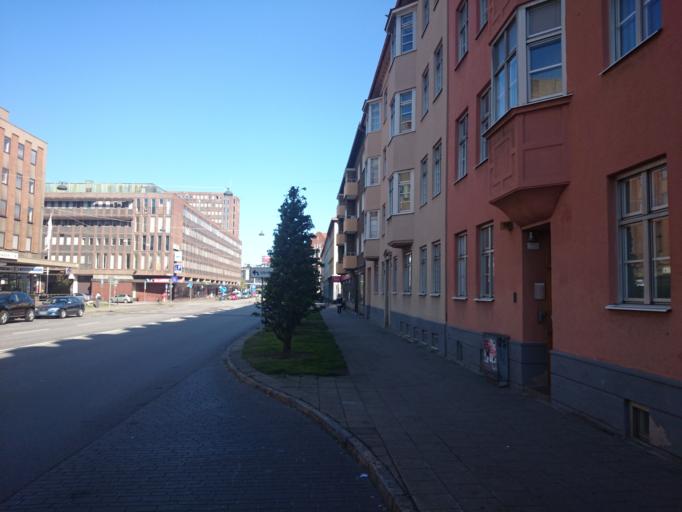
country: SE
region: Skane
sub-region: Malmo
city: Malmoe
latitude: 55.6041
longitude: 13.0272
